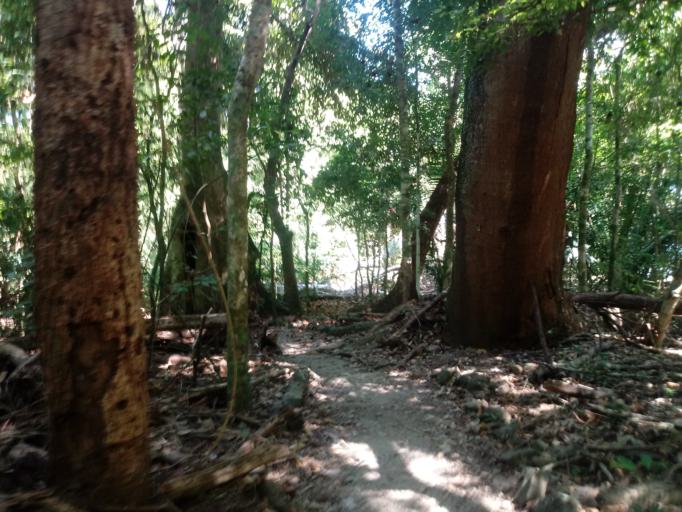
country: CR
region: Puntarenas
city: Paquera
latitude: 9.5865
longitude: -85.0934
